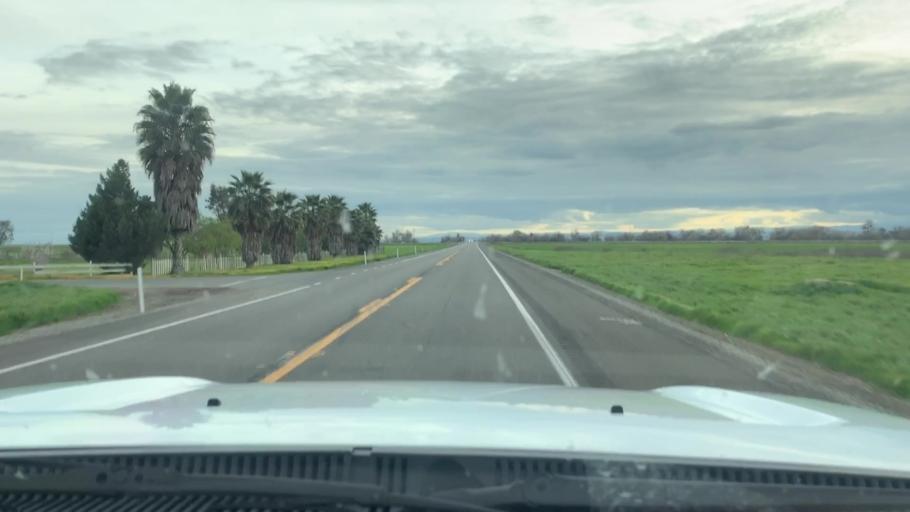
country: US
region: California
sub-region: Kings County
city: Stratford
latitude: 36.1860
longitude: -119.8305
